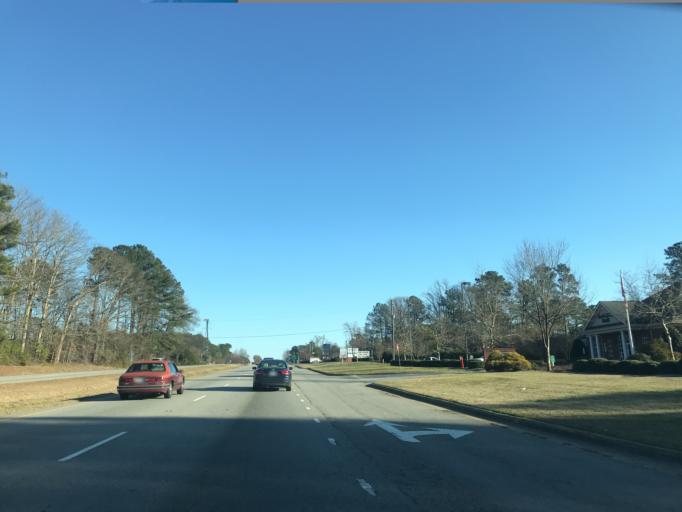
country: US
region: North Carolina
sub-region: Wake County
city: Garner
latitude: 35.7138
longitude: -78.6288
